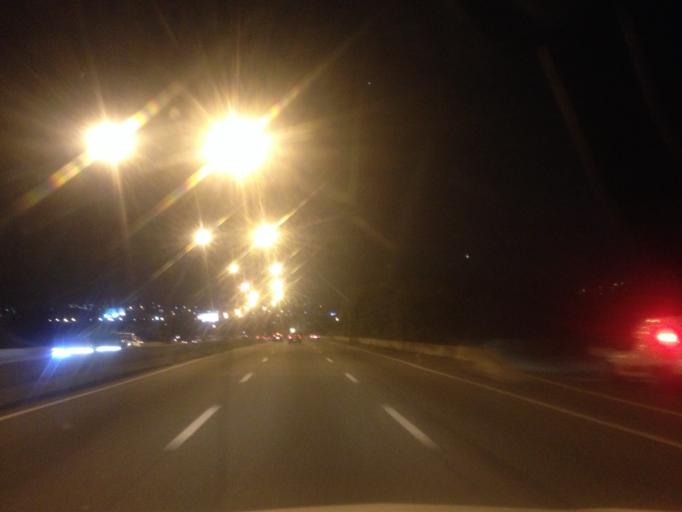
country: BR
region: Rio de Janeiro
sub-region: Duque De Caxias
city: Duque de Caxias
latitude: -22.7997
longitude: -43.3062
